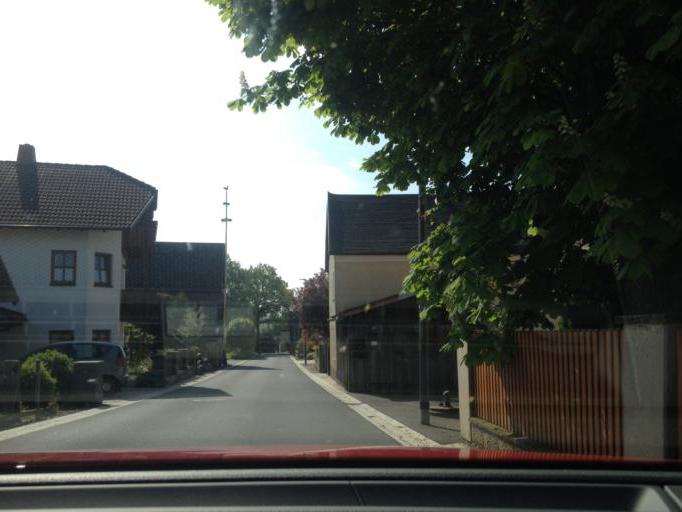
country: DE
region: Bavaria
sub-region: Upper Franconia
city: Thiersheim
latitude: 50.0349
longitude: 12.1318
